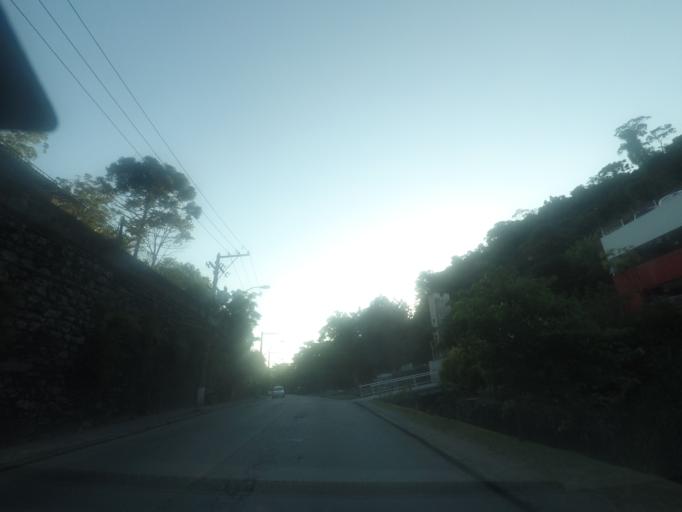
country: BR
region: Rio de Janeiro
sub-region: Petropolis
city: Petropolis
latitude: -22.5307
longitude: -43.1984
